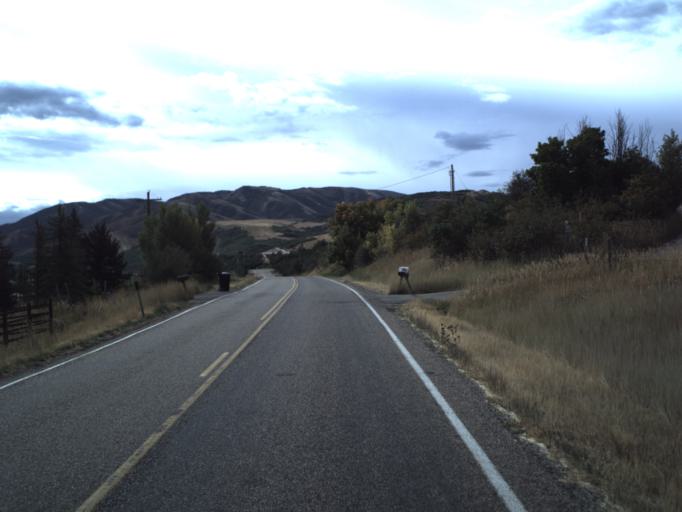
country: US
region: Utah
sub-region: Morgan County
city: Morgan
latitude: 40.9579
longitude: -111.6669
